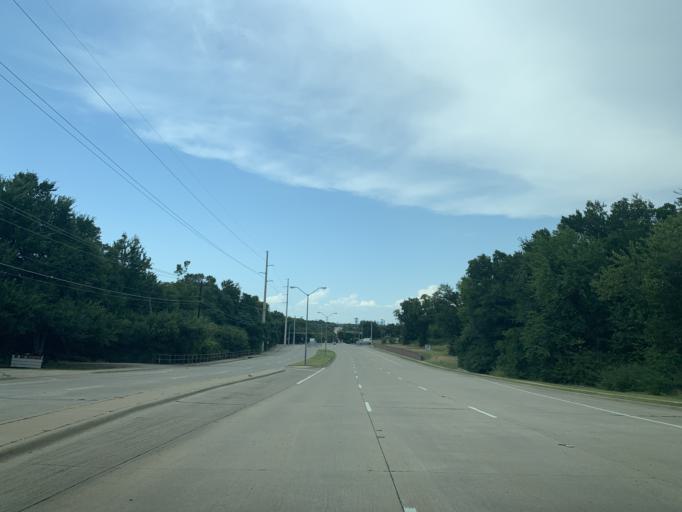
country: US
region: Texas
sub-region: Dallas County
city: Lancaster
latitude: 32.6600
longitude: -96.8056
